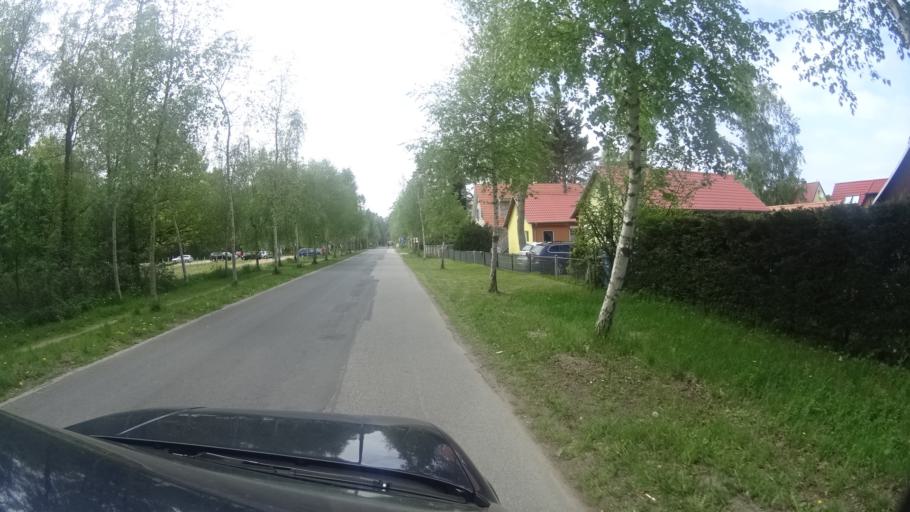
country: DE
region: Mecklenburg-Vorpommern
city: Ostseebad Dierhagen
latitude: 54.2816
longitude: 12.3182
